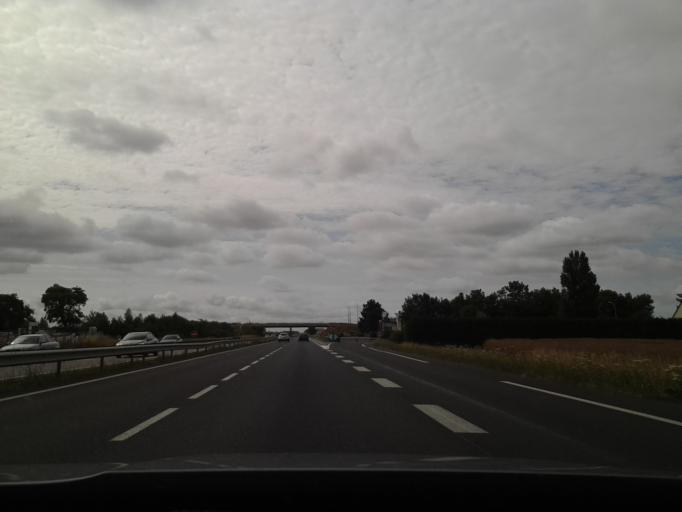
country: FR
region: Lower Normandy
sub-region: Departement du Calvados
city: Bretteville-sur-Laize
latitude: 49.0754
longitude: -0.2986
